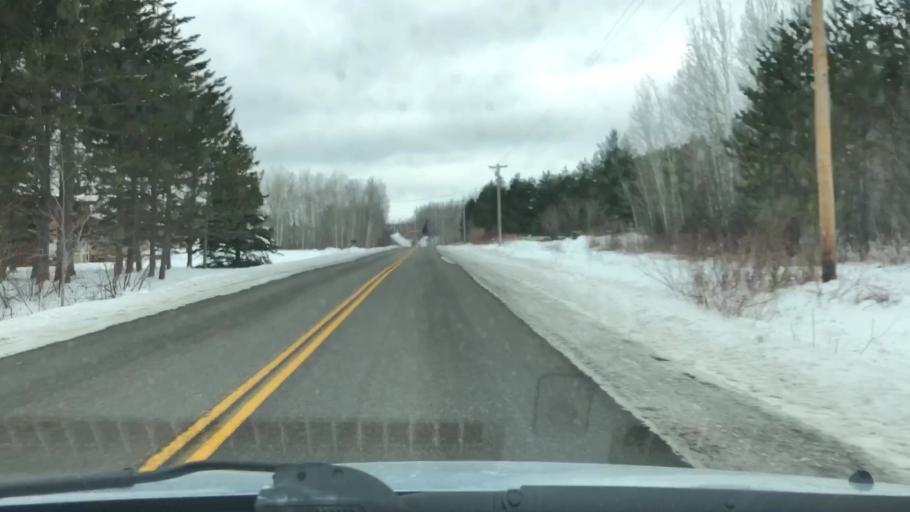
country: US
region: Minnesota
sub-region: Saint Louis County
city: Proctor
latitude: 46.7000
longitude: -92.2818
